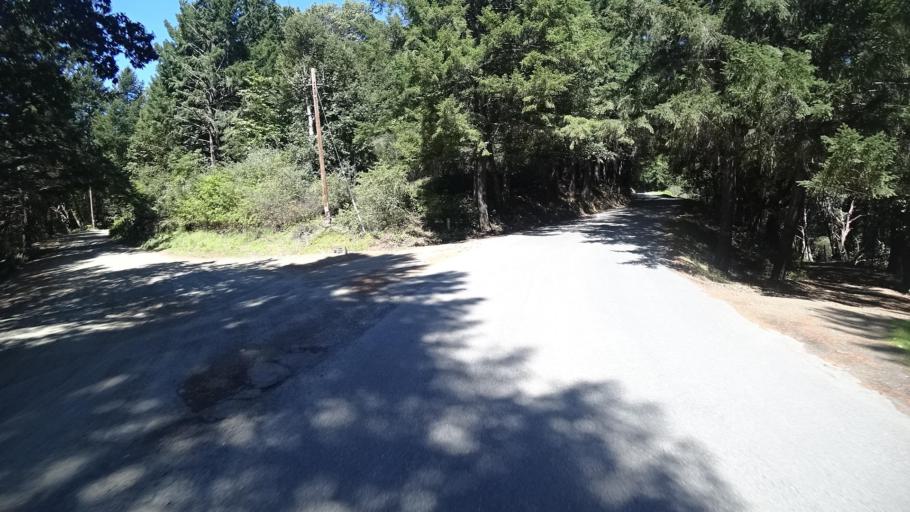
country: US
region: California
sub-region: Humboldt County
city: Redway
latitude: 40.0940
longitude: -123.9513
